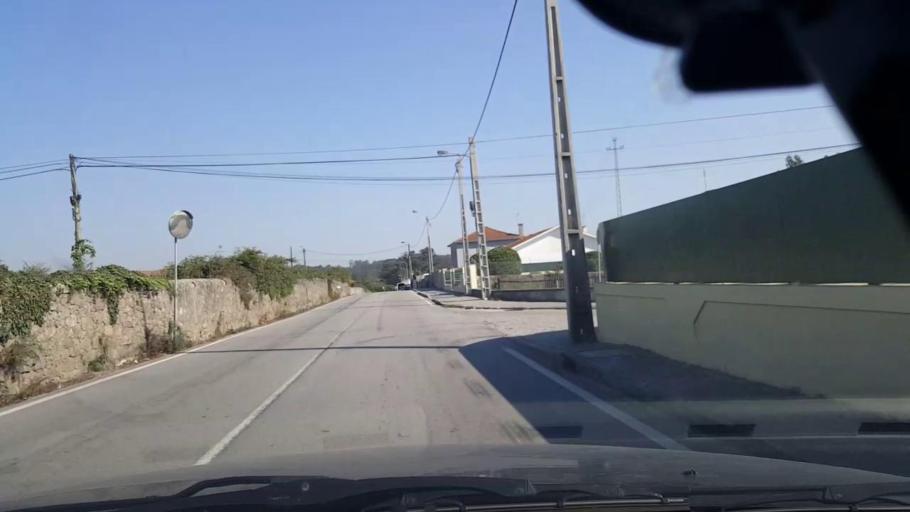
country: PT
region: Porto
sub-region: Vila do Conde
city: Arvore
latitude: 41.3449
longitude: -8.6797
